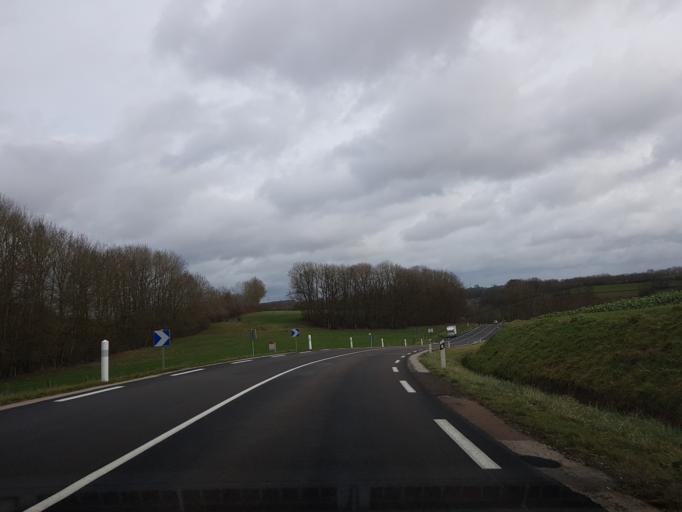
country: FR
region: Champagne-Ardenne
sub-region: Departement de la Haute-Marne
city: Langres
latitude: 47.8576
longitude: 5.3573
